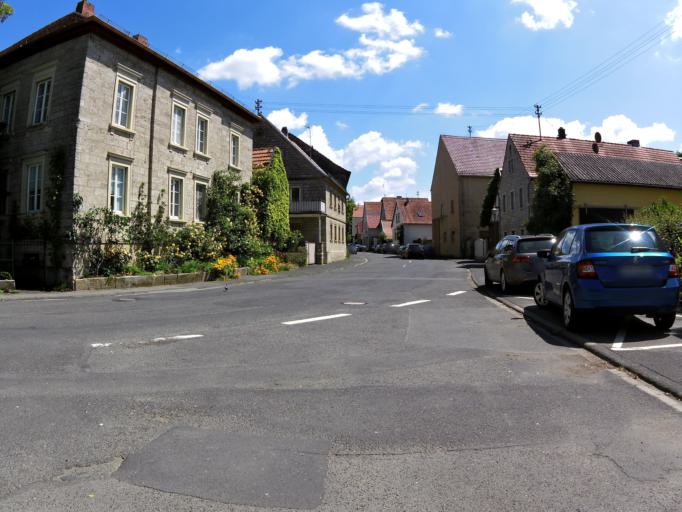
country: DE
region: Bavaria
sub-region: Regierungsbezirk Unterfranken
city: Theilheim
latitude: 49.7330
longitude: 10.0329
